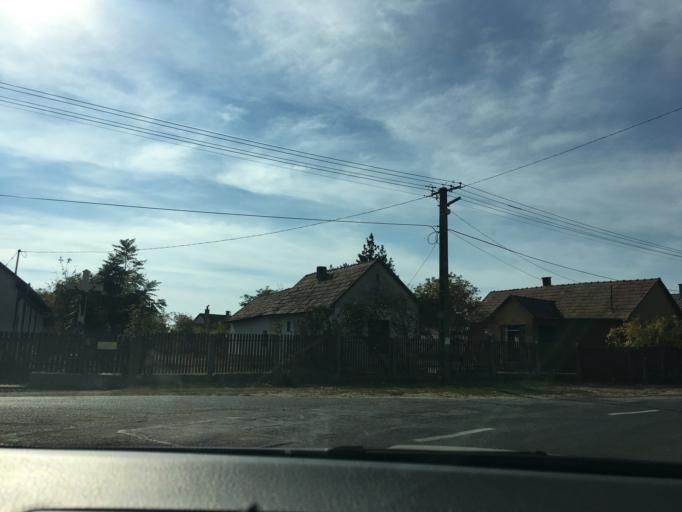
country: HU
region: Hajdu-Bihar
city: Nyirabrany
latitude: 47.5313
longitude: 21.9979
